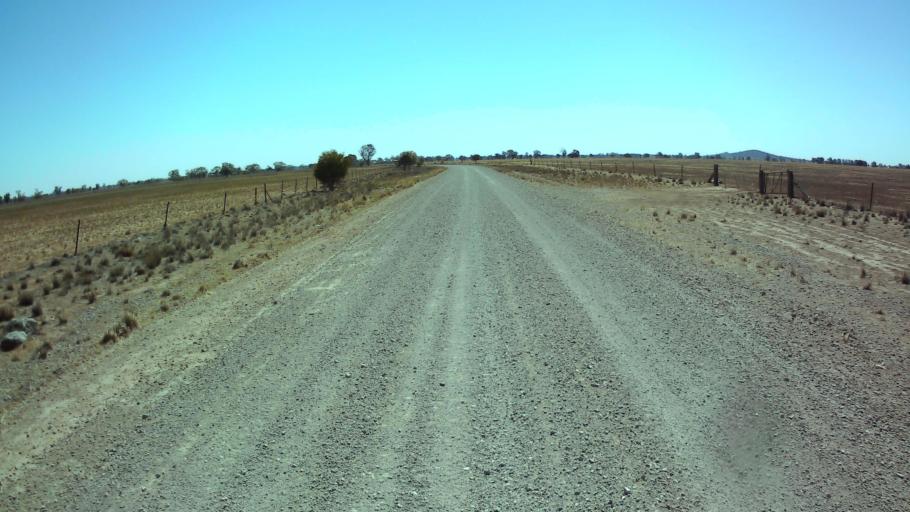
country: AU
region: New South Wales
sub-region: Forbes
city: Forbes
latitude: -33.7457
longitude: 147.7333
